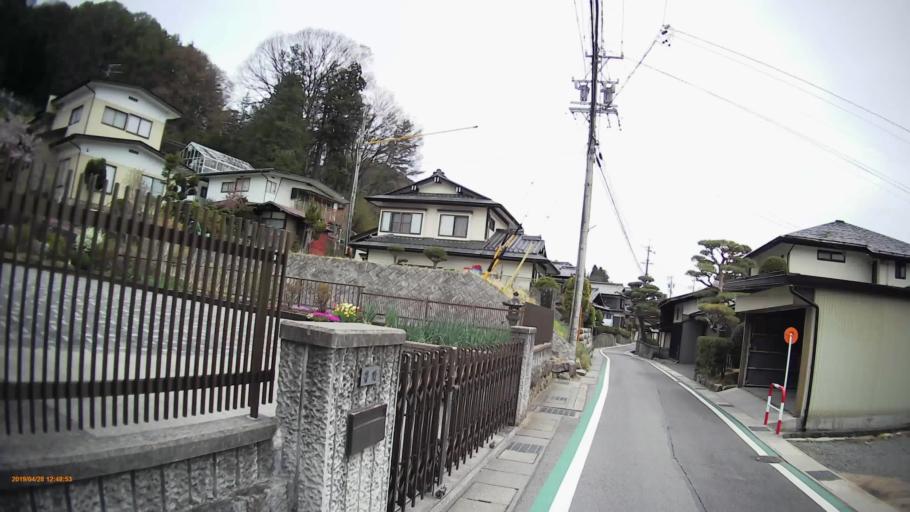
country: JP
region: Nagano
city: Chino
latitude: 36.0128
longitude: 138.1402
